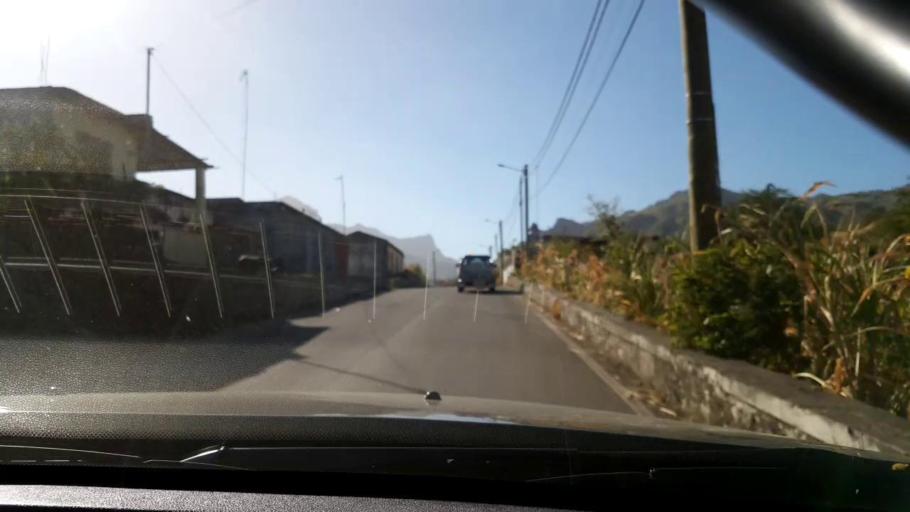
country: CV
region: Sao Lourenco dos Orgaos
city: Joao Teves
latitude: 15.0685
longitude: -23.5778
